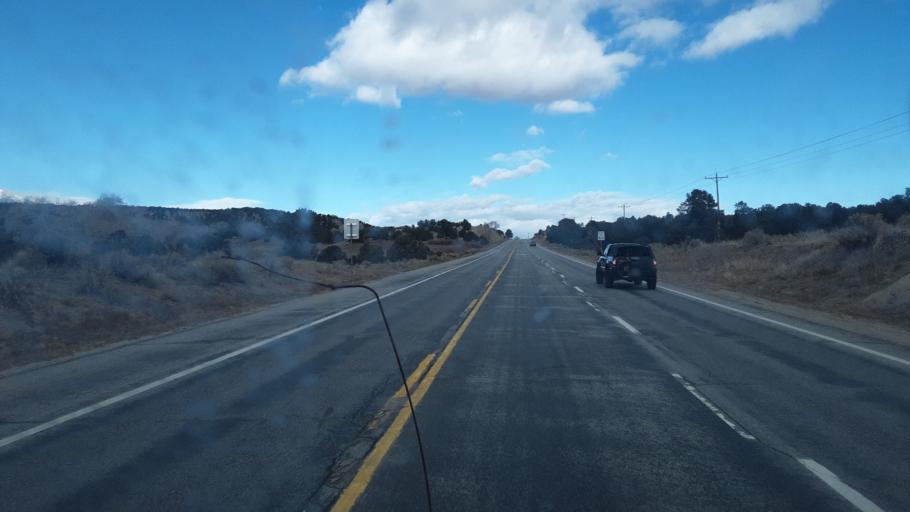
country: US
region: Colorado
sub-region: Chaffee County
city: Salida
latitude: 38.6680
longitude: -106.0898
